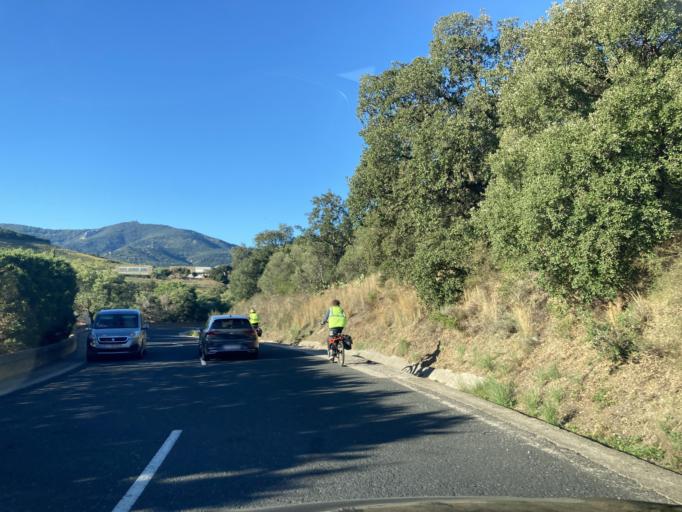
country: FR
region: Languedoc-Roussillon
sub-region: Departement des Pyrenees-Orientales
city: Collioure
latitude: 42.5258
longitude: 3.0703
